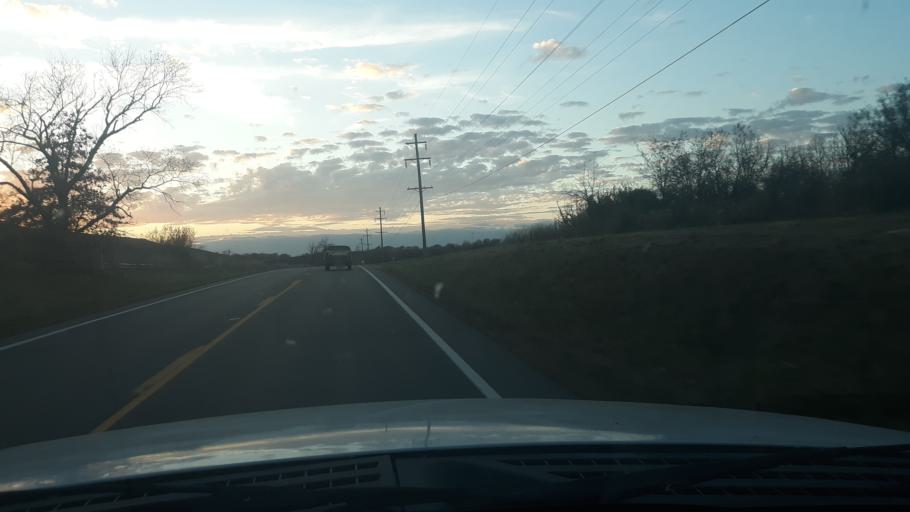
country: US
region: Illinois
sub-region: Saline County
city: Harrisburg
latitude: 37.8347
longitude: -88.5734
